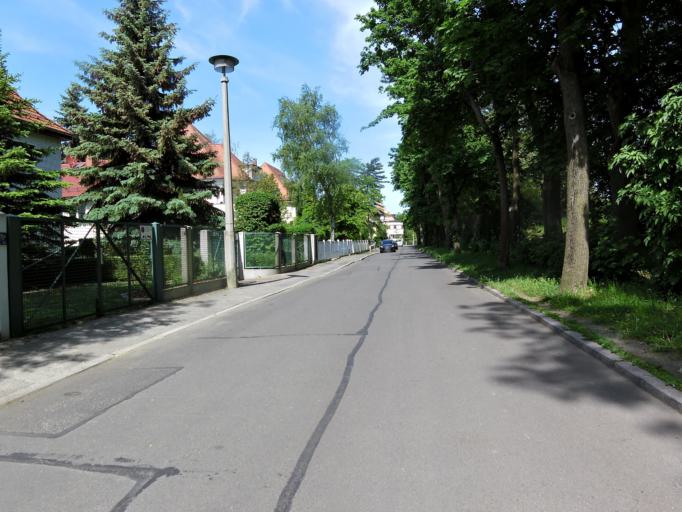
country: DE
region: Saxony
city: Leipzig
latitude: 51.3111
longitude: 12.4195
